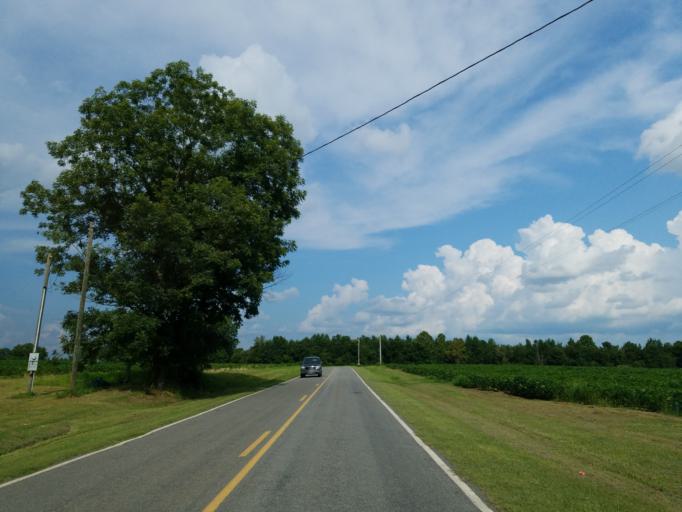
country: US
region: Georgia
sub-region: Dooly County
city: Unadilla
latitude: 32.1912
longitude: -83.7401
